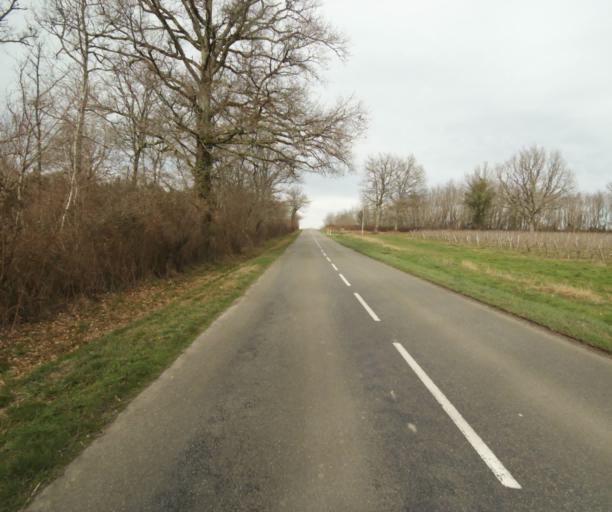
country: FR
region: Aquitaine
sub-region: Departement des Landes
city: Gabarret
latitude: 43.9573
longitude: 0.0076
